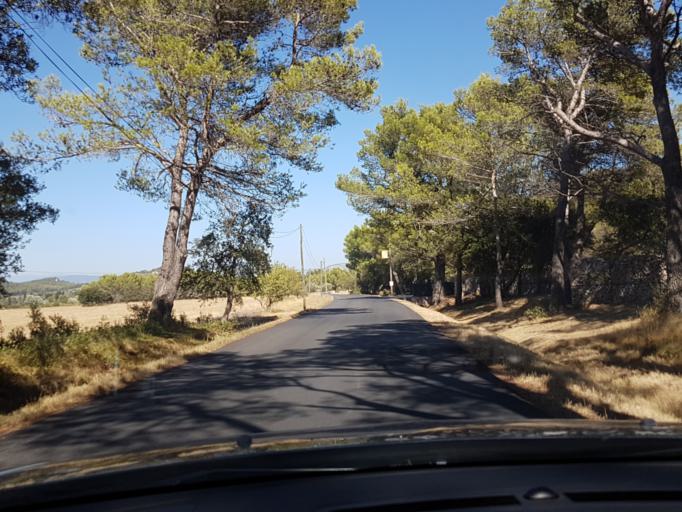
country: FR
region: Provence-Alpes-Cote d'Azur
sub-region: Departement des Bouches-du-Rhone
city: Eygalieres
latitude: 43.7696
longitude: 4.9851
